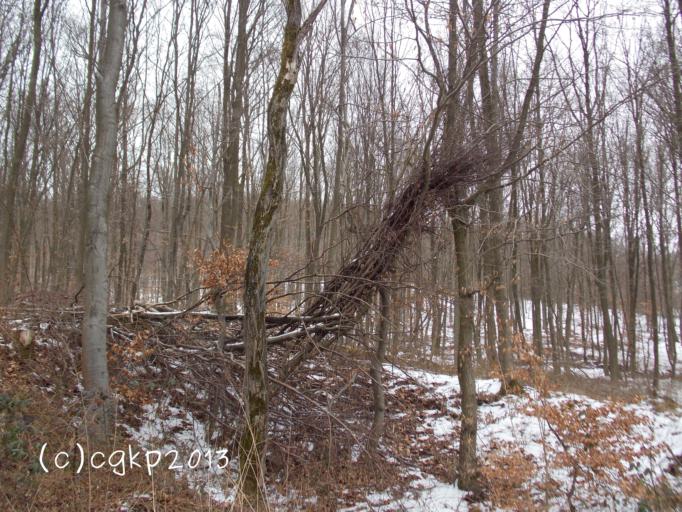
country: DE
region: Saarland
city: Hangard
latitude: 49.3600
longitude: 7.2113
